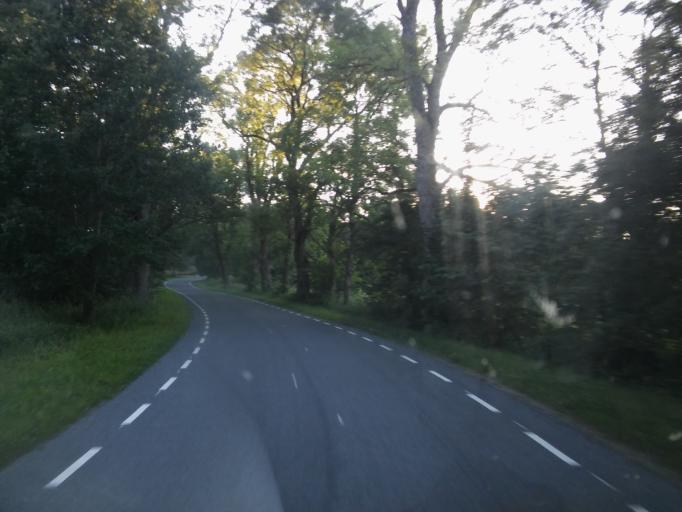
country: EE
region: Viljandimaa
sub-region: Abja vald
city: Abja-Paluoja
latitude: 58.2447
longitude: 25.3322
